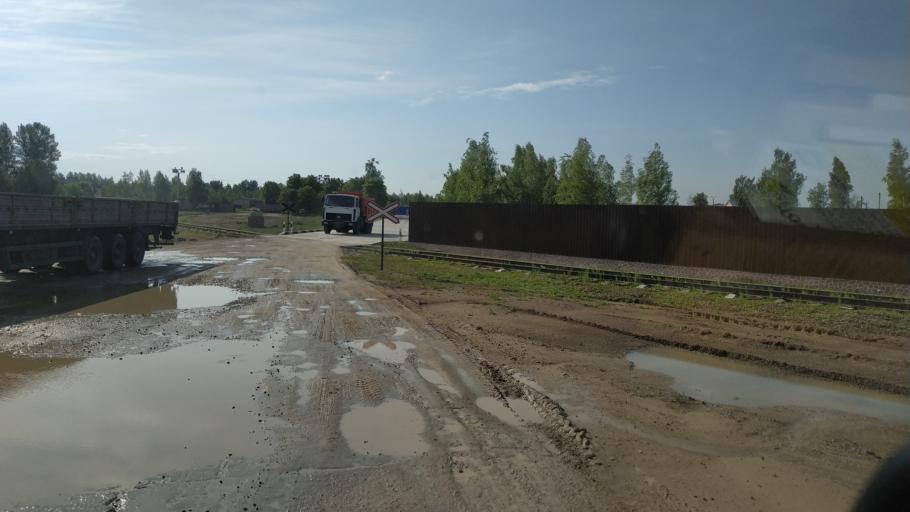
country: BY
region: Mogilev
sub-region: Mahilyowski Rayon
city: Veyno
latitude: 53.8394
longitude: 30.3838
